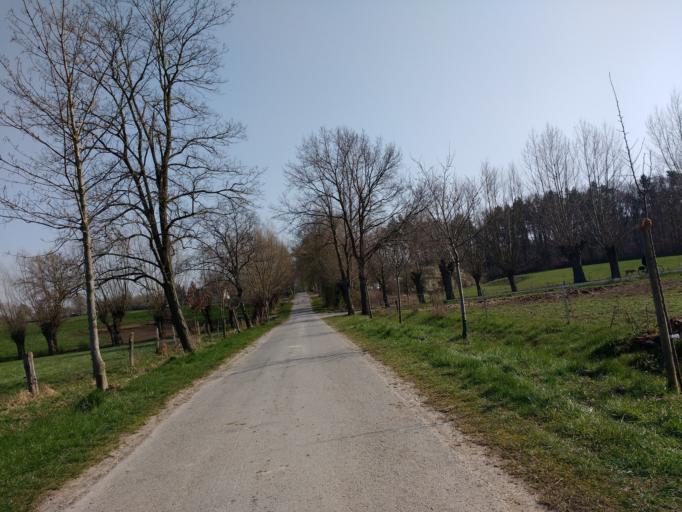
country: DE
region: North Rhine-Westphalia
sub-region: Regierungsbezirk Detmold
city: Salzkotten
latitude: 51.7231
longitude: 8.6373
